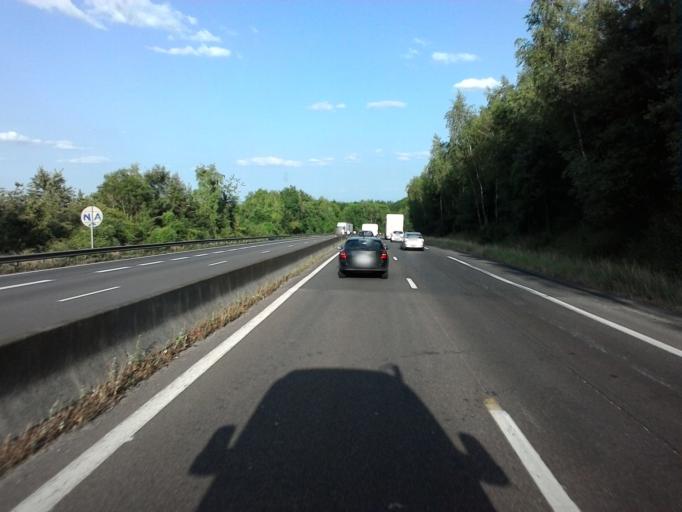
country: FR
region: Lorraine
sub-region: Departement de Meurthe-et-Moselle
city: Vandoeuvre-les-Nancy
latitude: 48.6419
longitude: 6.1659
